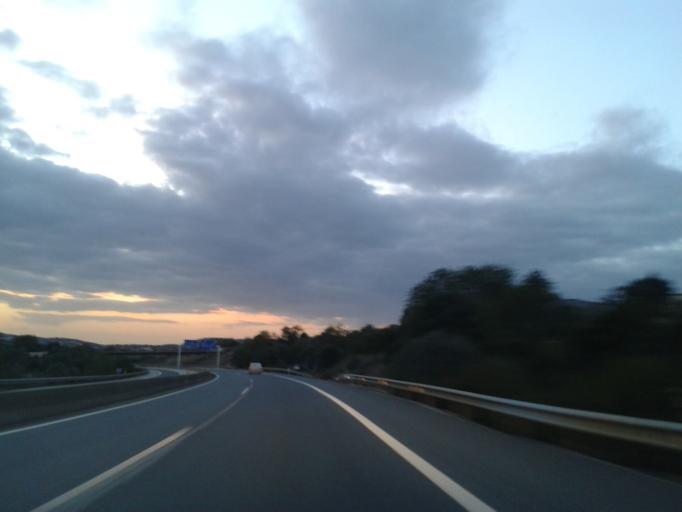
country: PT
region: Faro
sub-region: Loule
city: Boliqueime
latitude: 37.1619
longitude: -8.1923
